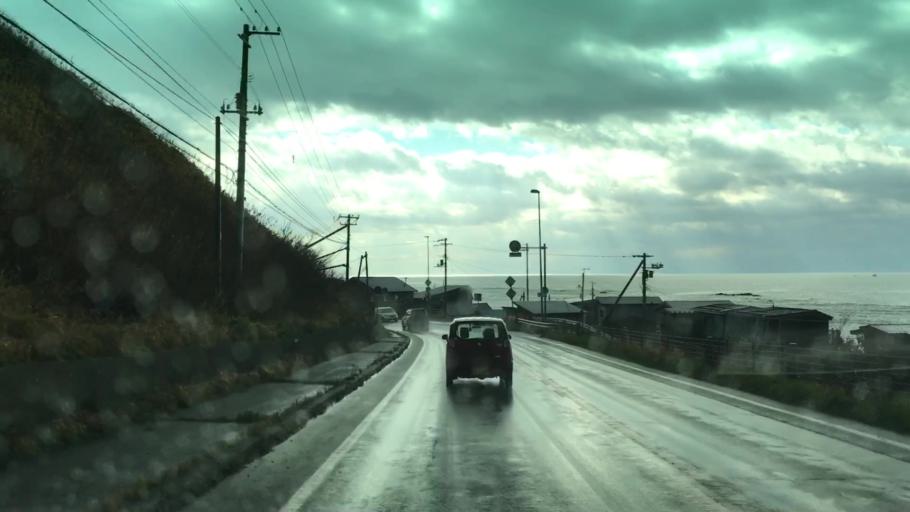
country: JP
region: Hokkaido
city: Shizunai-furukawacho
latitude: 42.1795
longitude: 142.7309
